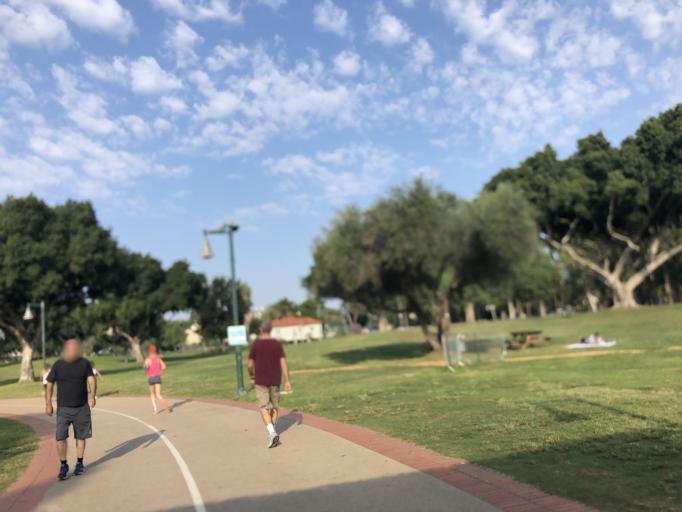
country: IL
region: Tel Aviv
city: Giv`atayim
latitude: 32.0520
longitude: 34.8251
